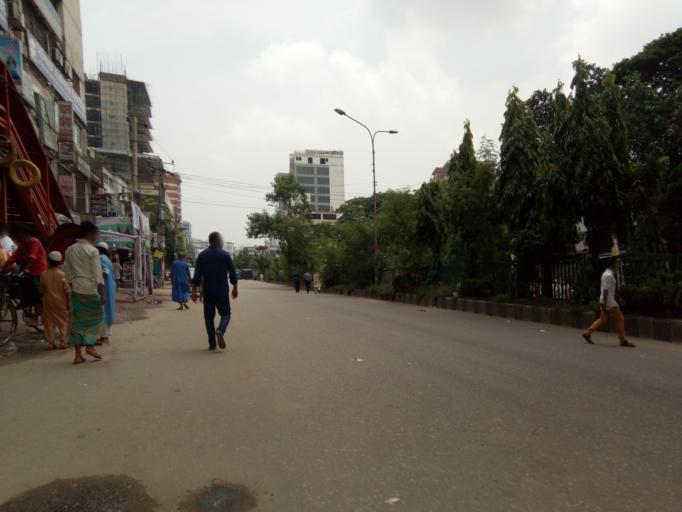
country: BD
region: Dhaka
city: Azimpur
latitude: 23.7482
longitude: 90.3795
